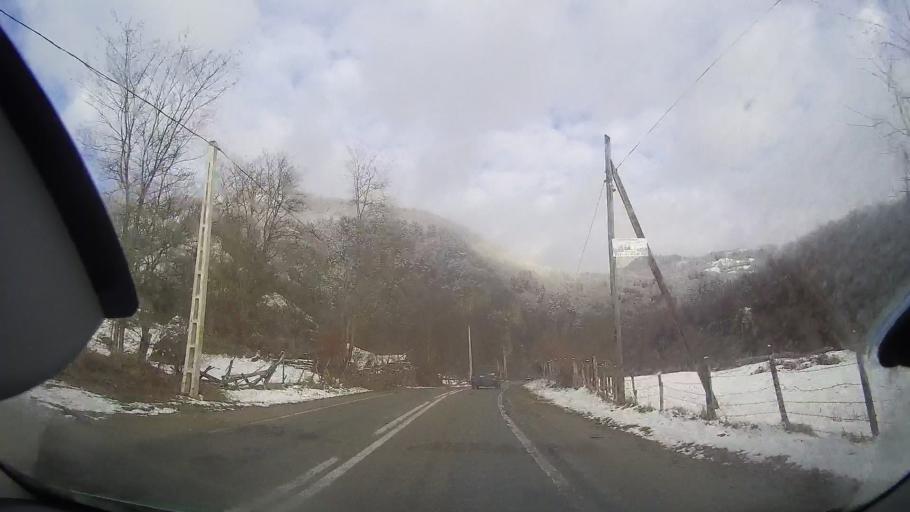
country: RO
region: Alba
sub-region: Oras Baia de Aries
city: Baia de Aries
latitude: 46.3978
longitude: 23.3005
